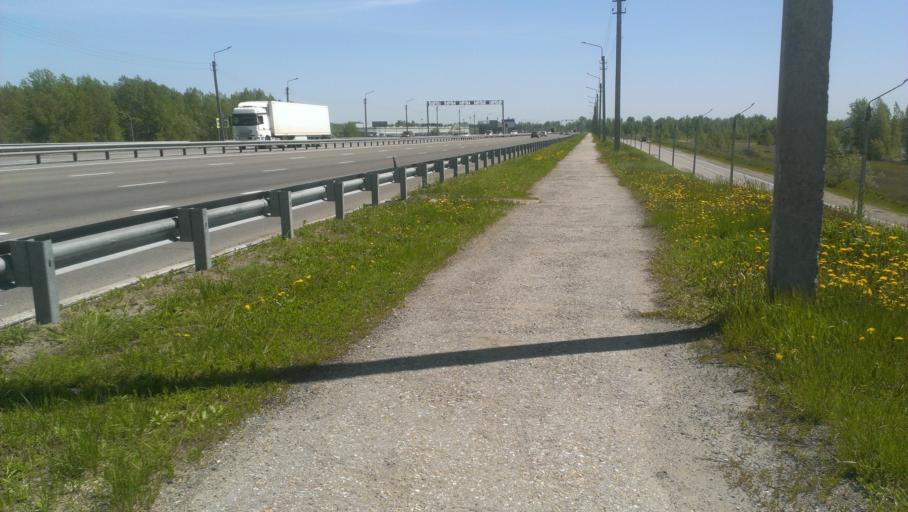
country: RU
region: Altai Krai
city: Zaton
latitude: 53.3190
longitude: 83.8156
